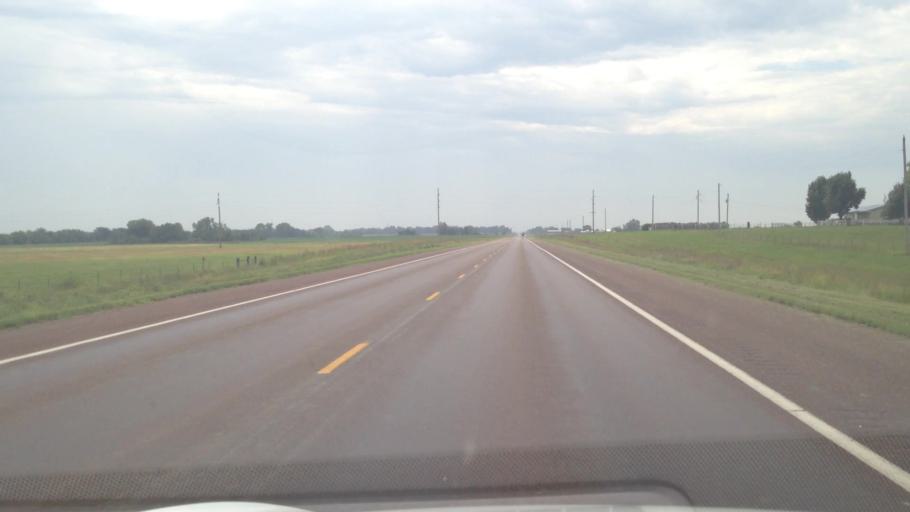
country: US
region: Kansas
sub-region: Crawford County
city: Girard
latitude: 37.4600
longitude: -94.8330
